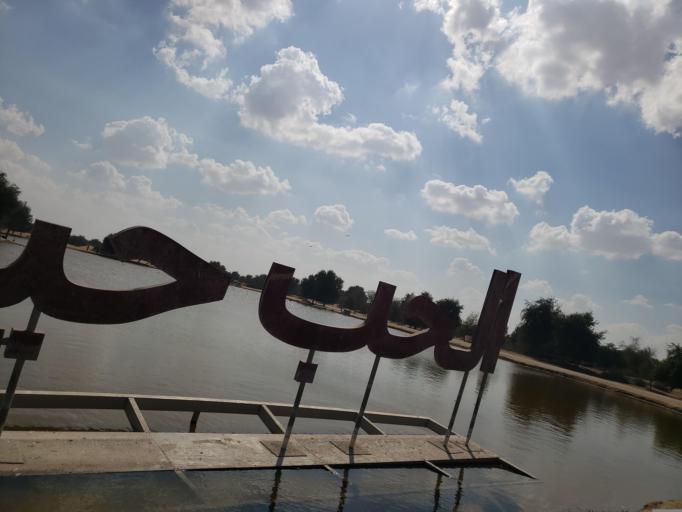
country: AE
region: Dubai
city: Dubai
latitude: 24.8354
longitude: 55.3755
